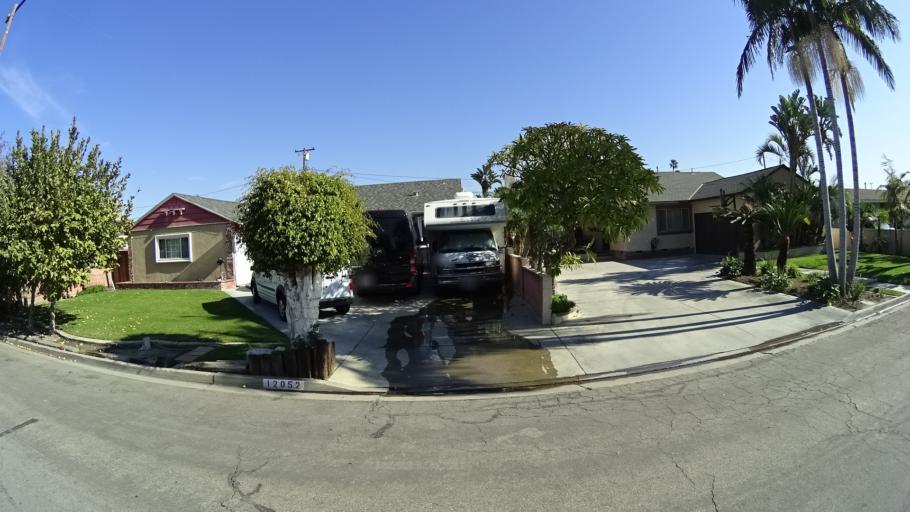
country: US
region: California
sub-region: Orange County
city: Garden Grove
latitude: 33.7878
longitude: -117.9285
